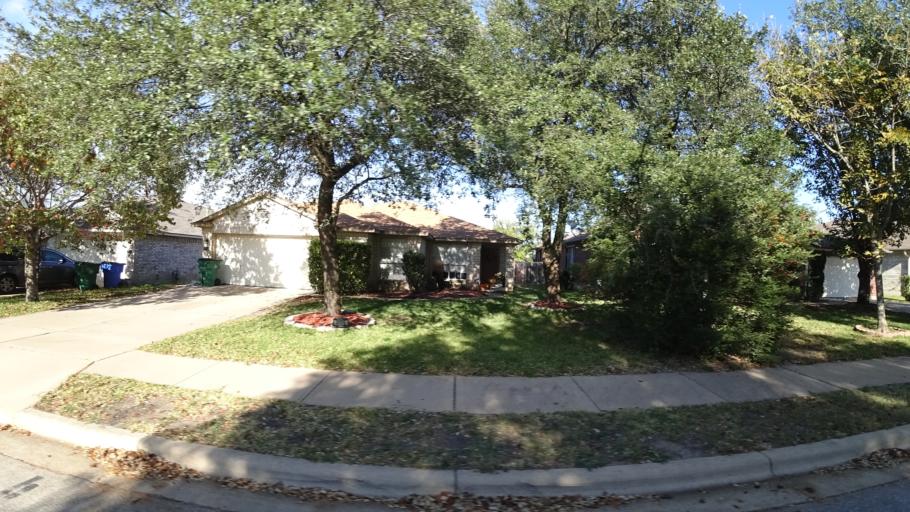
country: US
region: Texas
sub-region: Travis County
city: Wells Branch
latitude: 30.4633
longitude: -97.6897
